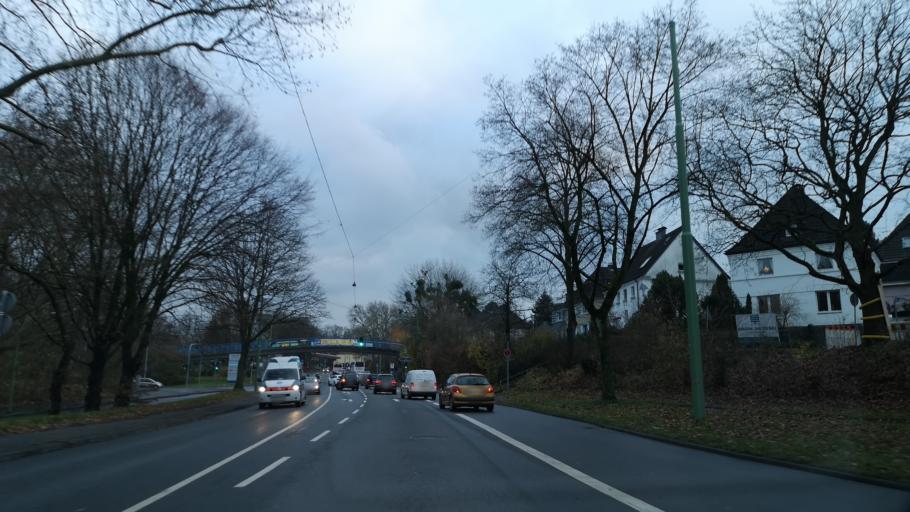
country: DE
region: North Rhine-Westphalia
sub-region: Regierungsbezirk Arnsberg
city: Hagen
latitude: 51.3714
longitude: 7.4729
